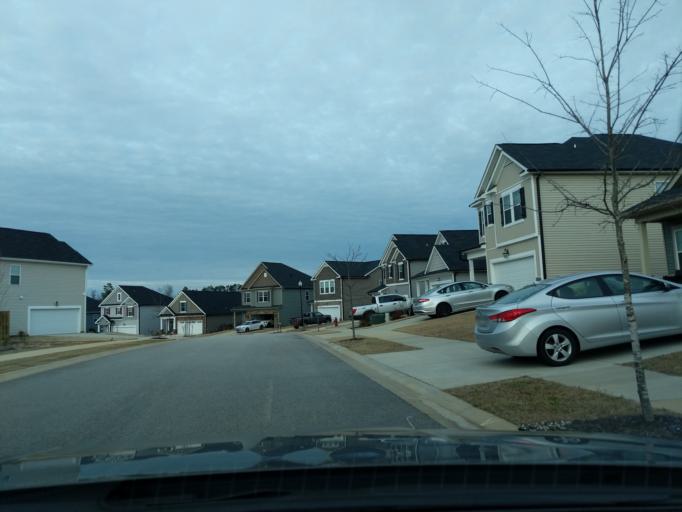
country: US
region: Georgia
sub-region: Columbia County
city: Grovetown
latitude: 33.4686
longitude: -82.1990
